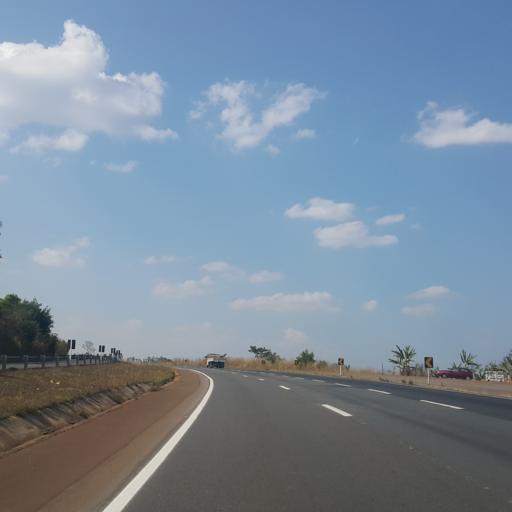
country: BR
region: Goias
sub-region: Abadiania
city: Abadiania
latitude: -16.2958
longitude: -48.8024
